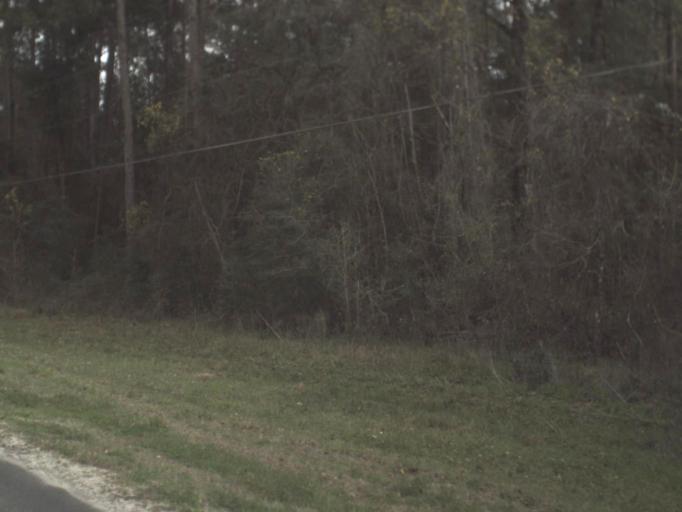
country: US
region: Florida
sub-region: Leon County
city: Woodville
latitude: 30.2352
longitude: -84.2439
